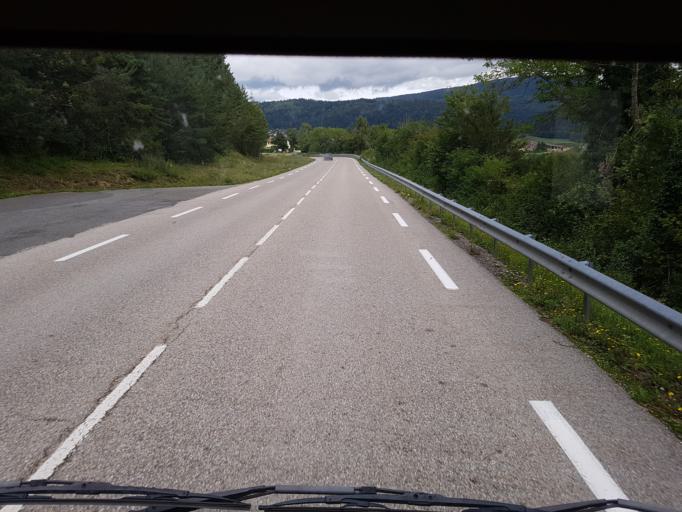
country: FR
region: Rhone-Alpes
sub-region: Departement de l'Ain
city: Saint-Martin-du-Frene
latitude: 46.1251
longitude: 5.5303
